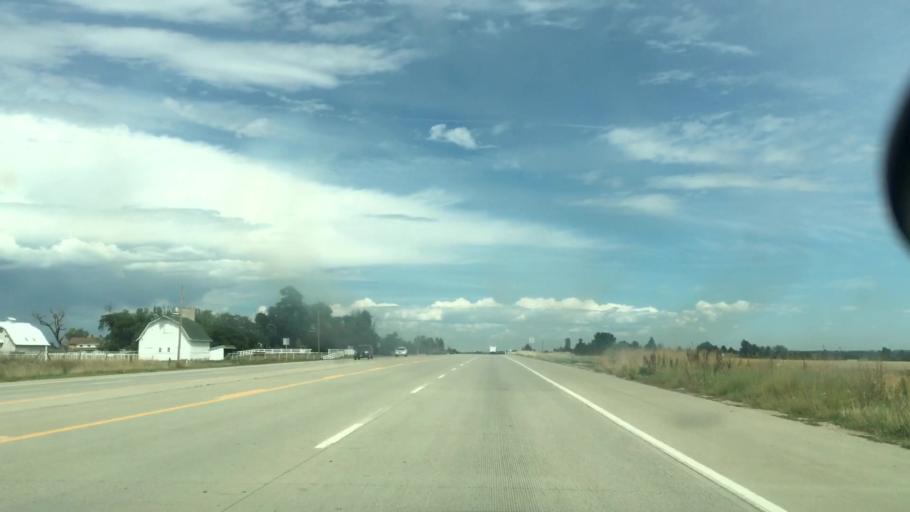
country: US
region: Colorado
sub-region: Larimer County
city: Berthoud
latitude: 40.2637
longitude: -105.1024
